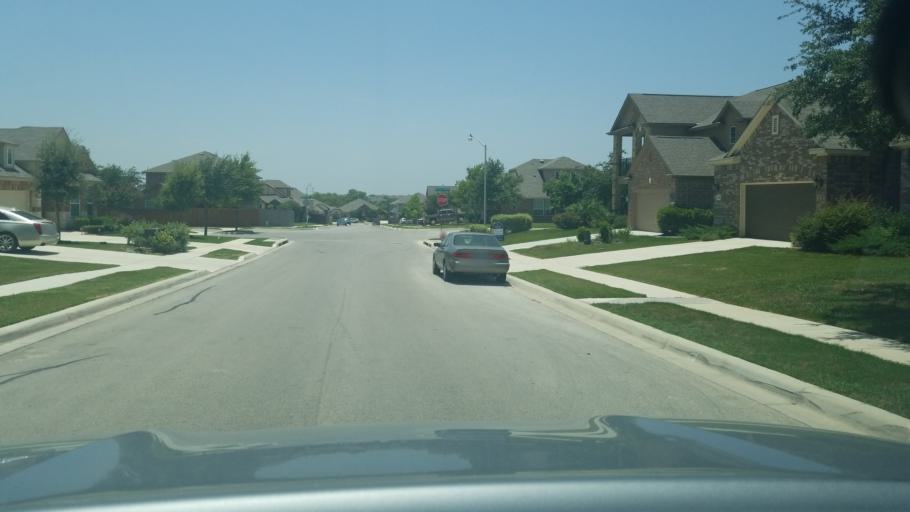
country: US
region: Texas
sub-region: Guadalupe County
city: Cibolo
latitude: 29.5808
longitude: -98.2305
